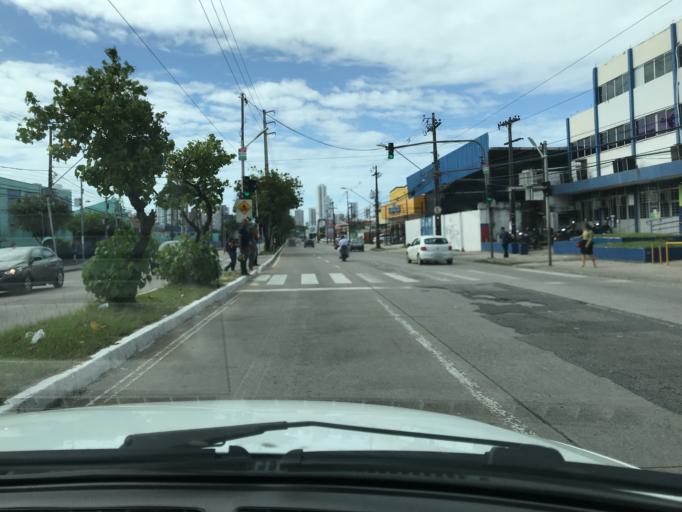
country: BR
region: Pernambuco
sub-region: Recife
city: Recife
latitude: -8.0624
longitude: -34.9176
